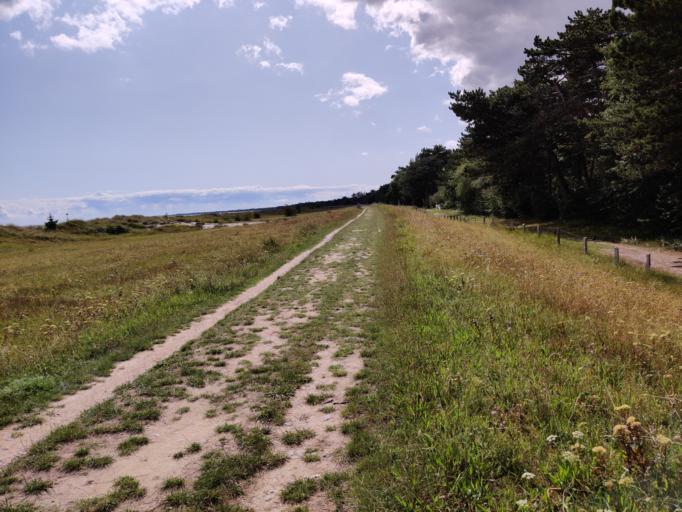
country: DK
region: Zealand
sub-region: Guldborgsund Kommune
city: Nykobing Falster
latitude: 54.7010
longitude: 11.9770
